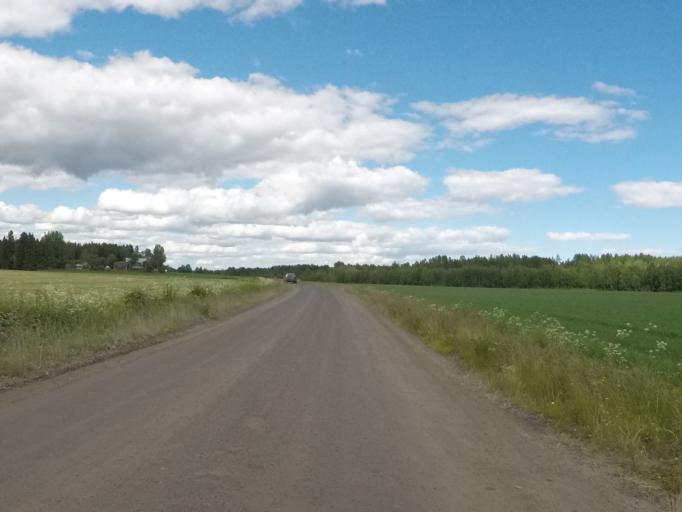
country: SE
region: Vaesterbotten
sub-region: Robertsfors Kommun
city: Robertsfors
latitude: 64.0846
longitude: 20.8736
